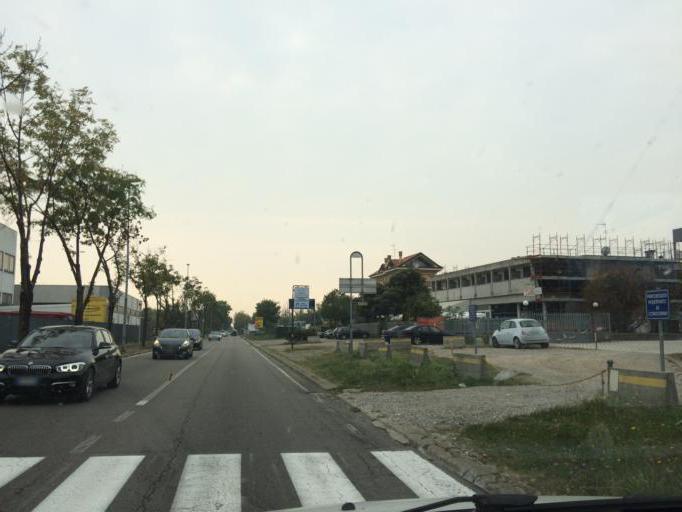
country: IT
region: Lombardy
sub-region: Provincia di Varese
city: Castellanza
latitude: 45.5983
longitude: 8.8955
